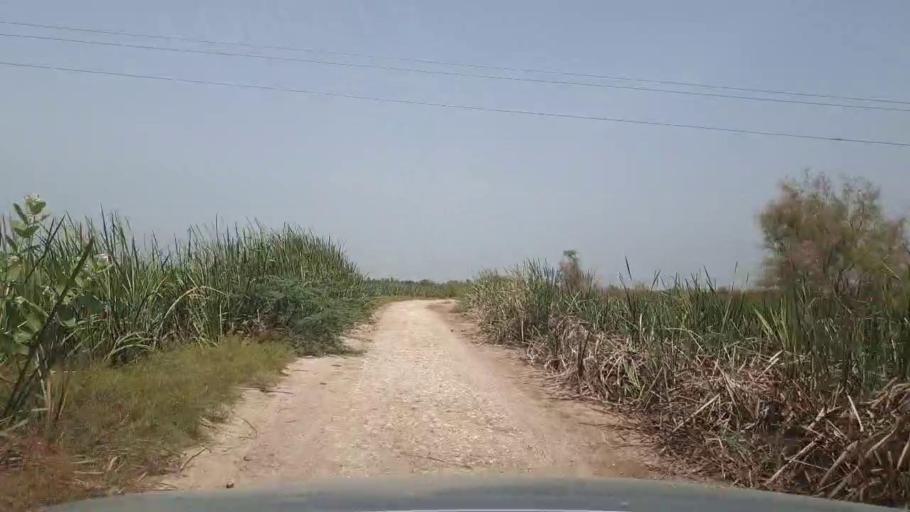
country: PK
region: Sindh
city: Garhi Yasin
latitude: 27.9499
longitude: 68.4320
